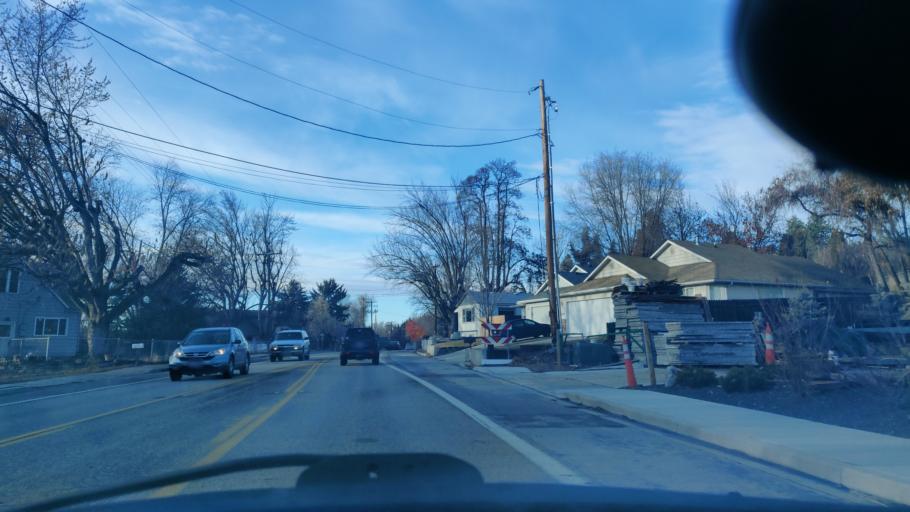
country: US
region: Idaho
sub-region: Ada County
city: Garden City
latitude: 43.6456
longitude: -116.2176
